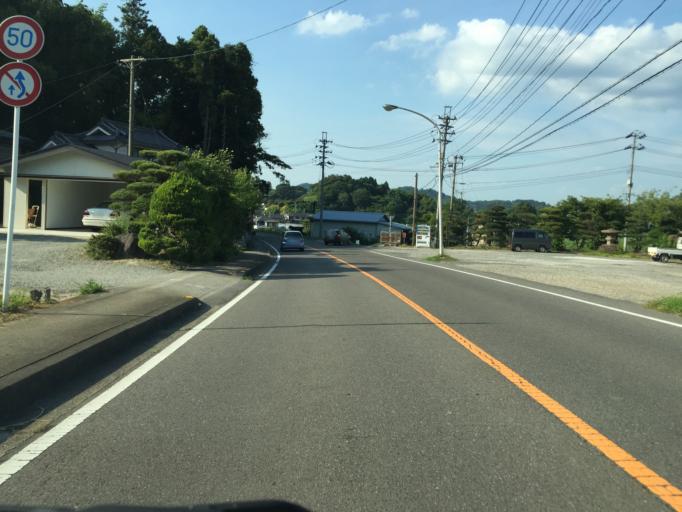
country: JP
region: Fukushima
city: Nihommatsu
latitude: 37.5752
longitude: 140.4171
